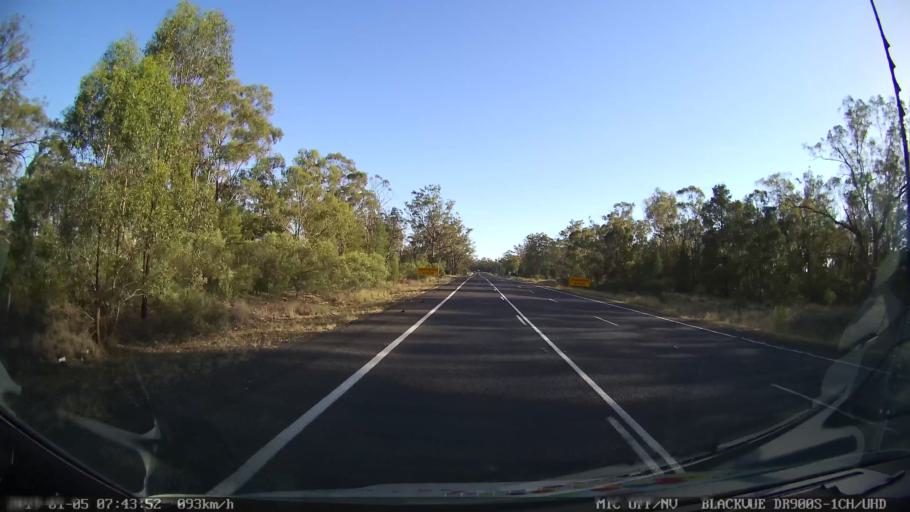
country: AU
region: New South Wales
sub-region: Gilgandra
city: Gilgandra
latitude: -31.8798
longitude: 148.6367
